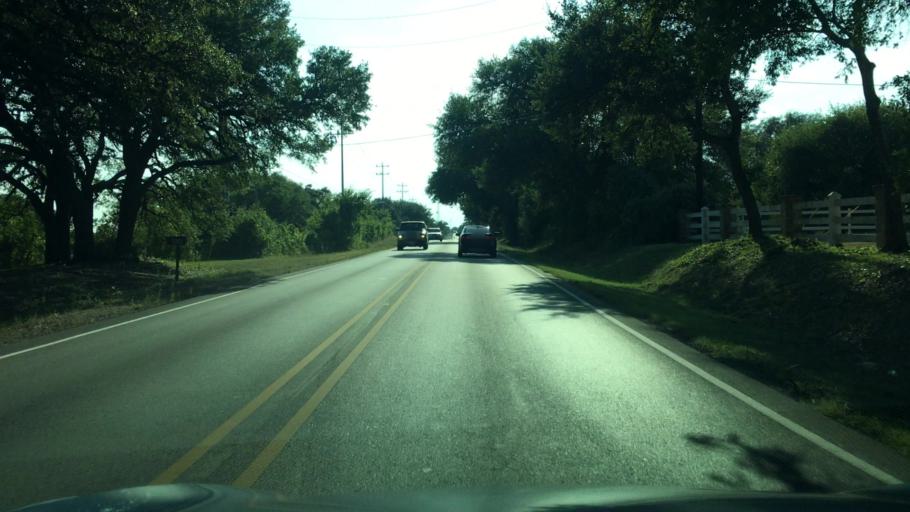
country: US
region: Texas
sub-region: Travis County
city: Shady Hollow
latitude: 30.1173
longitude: -97.9750
